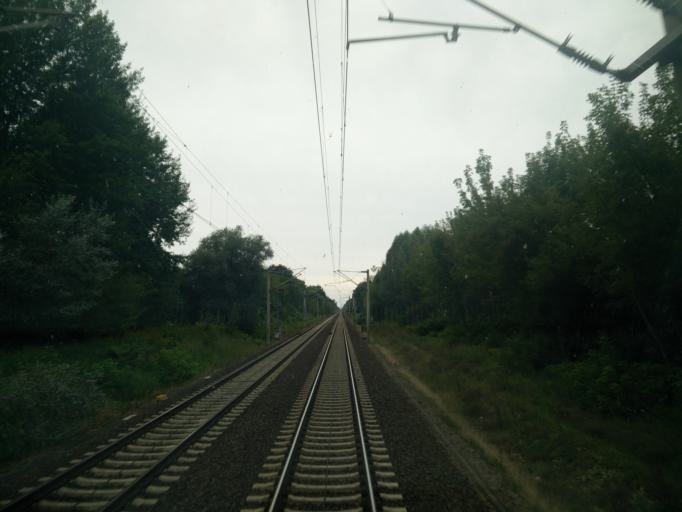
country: DE
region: Brandenburg
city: Dallgow-Doeberitz
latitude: 52.5662
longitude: 13.0648
